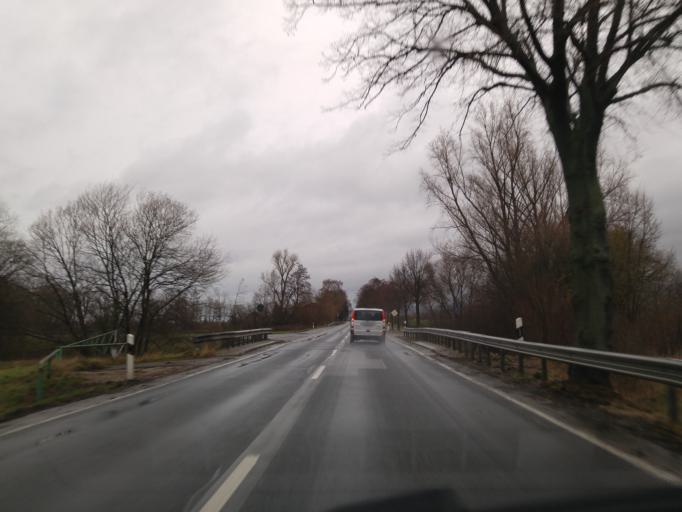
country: DE
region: Lower Saxony
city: Rosdorf
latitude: 51.4917
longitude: 9.9359
